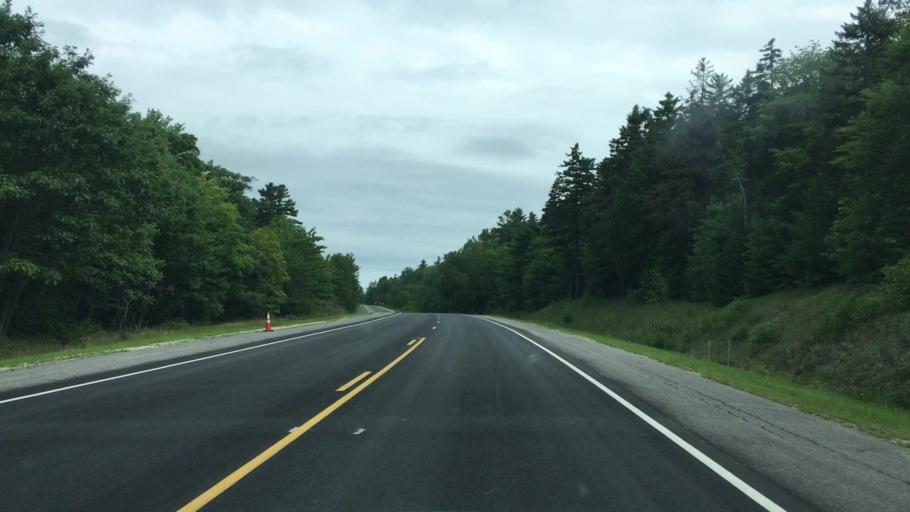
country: US
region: Maine
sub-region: Washington County
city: Cherryfield
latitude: 44.8980
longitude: -67.8556
